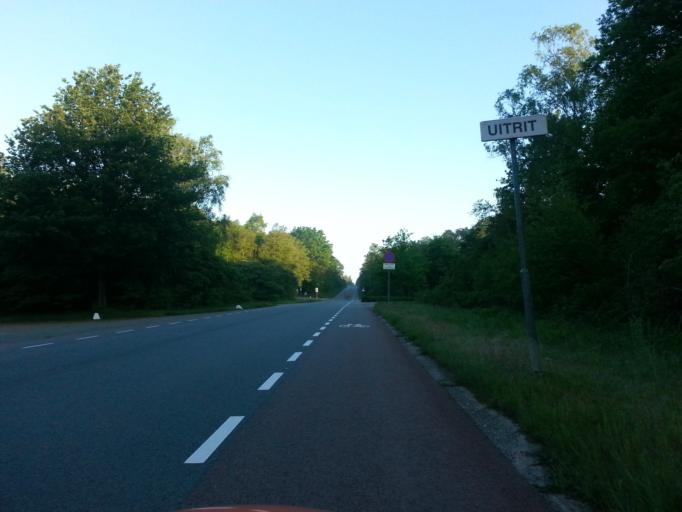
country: NL
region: Utrecht
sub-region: Gemeente Amersfoort
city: Amersfoort
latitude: 52.1226
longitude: 5.3544
